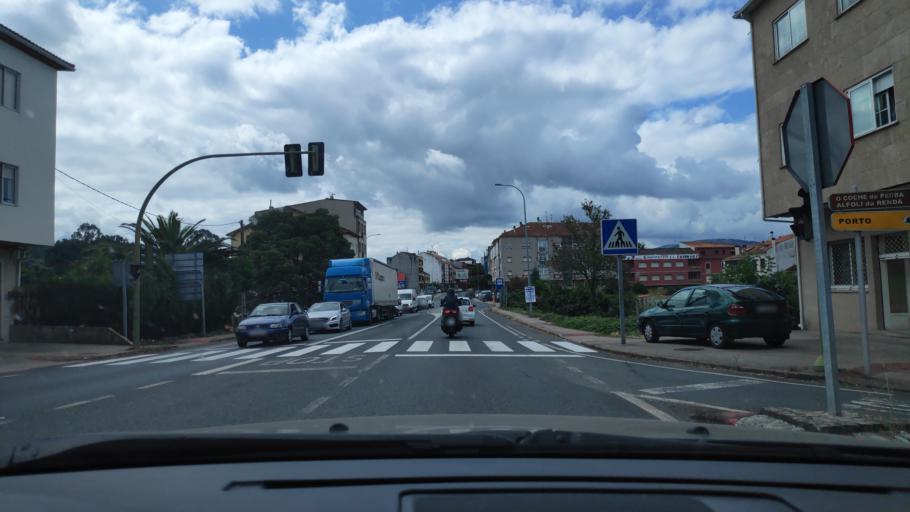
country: ES
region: Galicia
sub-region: Provincia da Coruna
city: Padron
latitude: 42.7194
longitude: -8.6510
